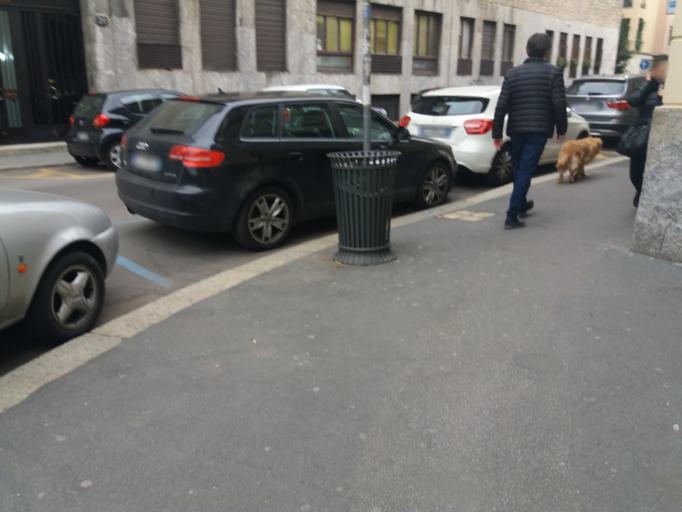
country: IT
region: Lombardy
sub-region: Citta metropolitana di Milano
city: Milano
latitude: 45.4542
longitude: 9.1939
